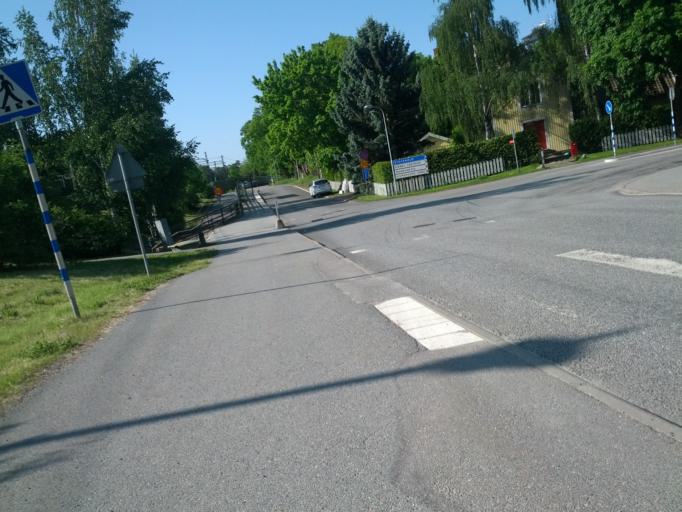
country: SE
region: Stockholm
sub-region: Danderyds Kommun
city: Djursholm
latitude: 59.3991
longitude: 18.0586
